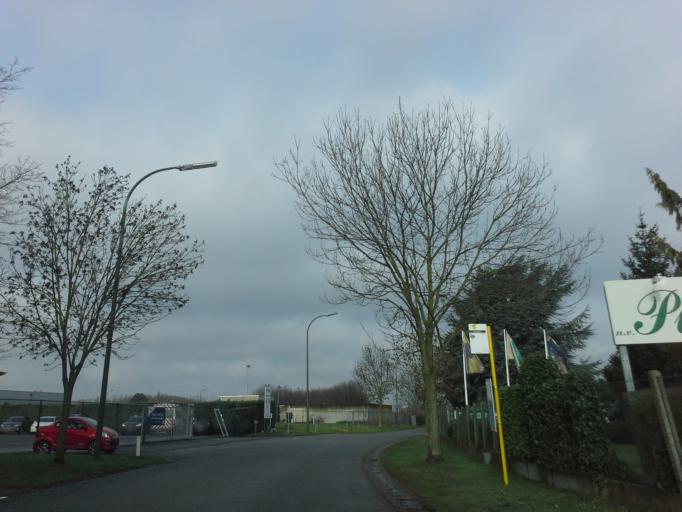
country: BE
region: Flanders
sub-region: Provincie Limburg
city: Sint-Truiden
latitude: 50.8198
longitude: 5.2033
